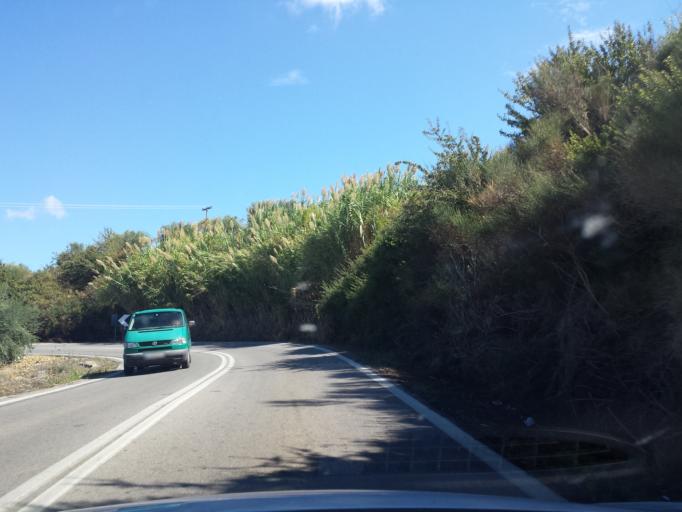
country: GR
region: Peloponnese
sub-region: Nomos Messinias
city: Pylos
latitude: 36.9419
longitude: 21.7474
